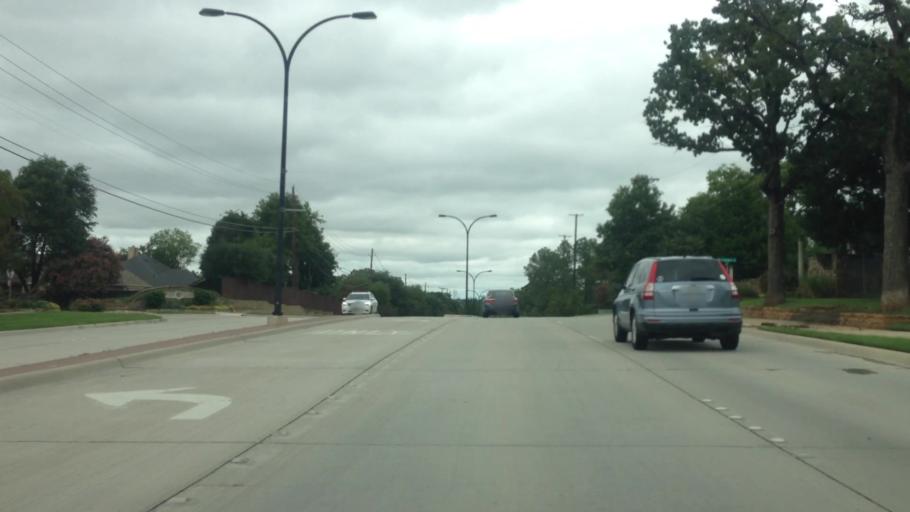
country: US
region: Texas
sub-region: Tarrant County
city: Keller
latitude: 32.9158
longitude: -97.2322
